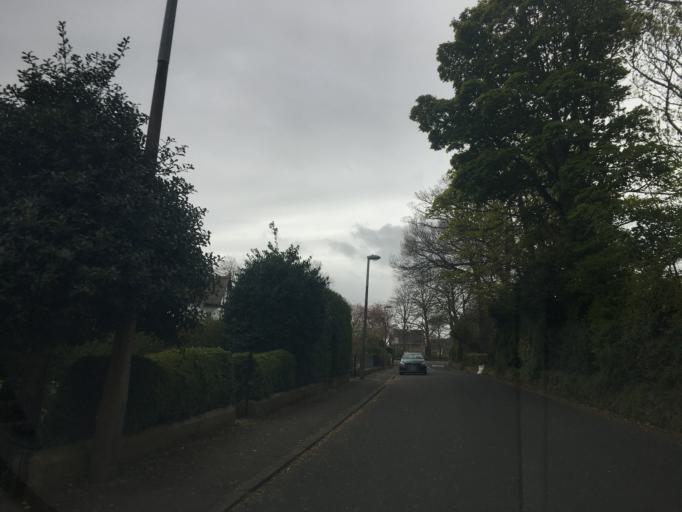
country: GB
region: Scotland
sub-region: Edinburgh
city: Colinton
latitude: 55.9137
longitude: -3.2459
